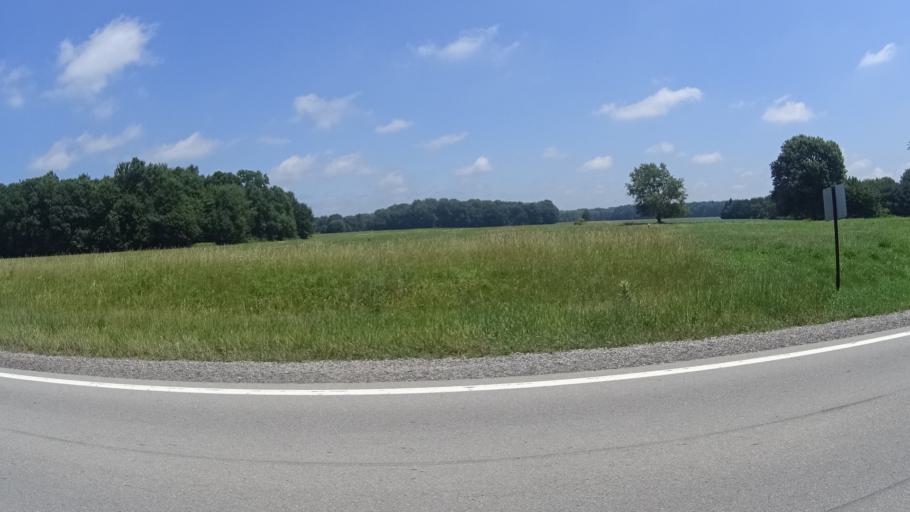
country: US
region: Ohio
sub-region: Lorain County
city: Vermilion
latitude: 41.3580
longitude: -82.3594
